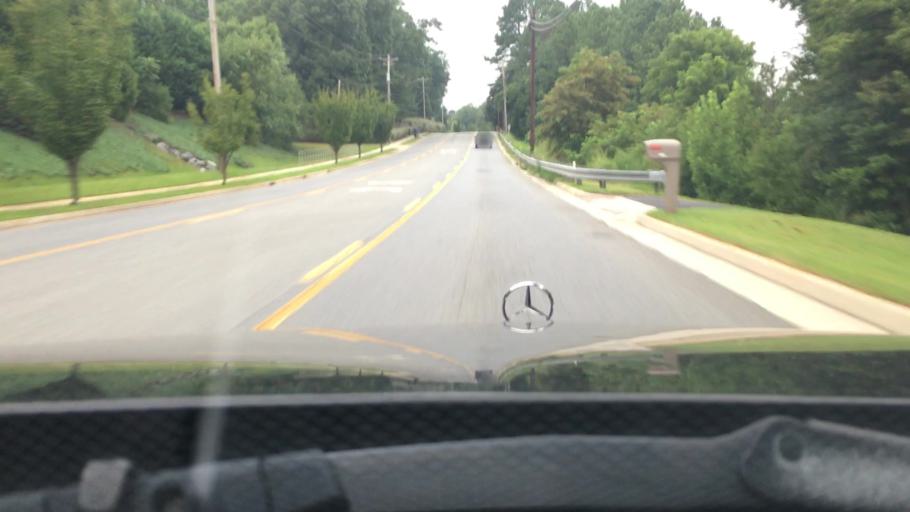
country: US
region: Virginia
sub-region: Campbell County
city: Timberlake
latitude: 37.3581
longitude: -79.2276
